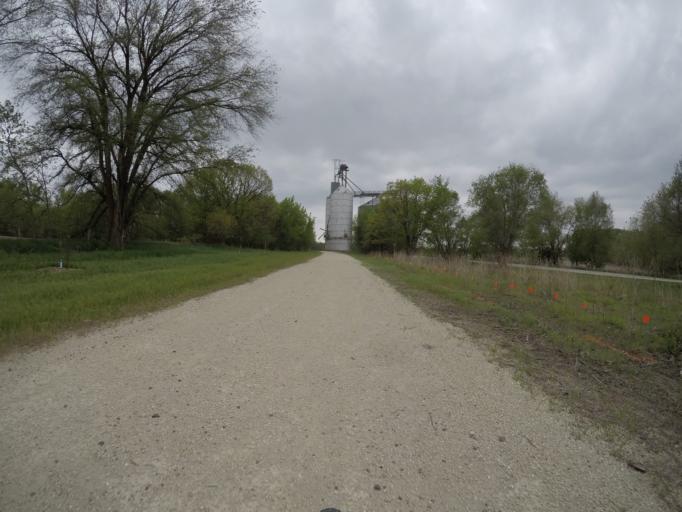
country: US
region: Nebraska
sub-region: Gage County
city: Wymore
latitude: 40.1384
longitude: -96.6443
